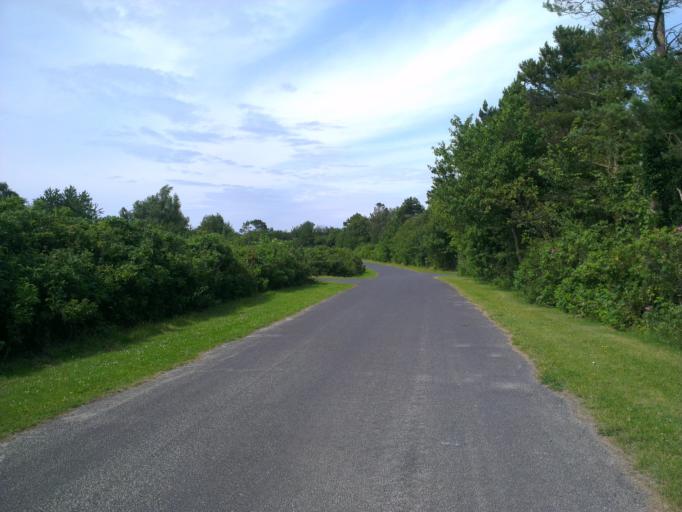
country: DK
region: Capital Region
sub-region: Halsnaes Kommune
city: Hundested
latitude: 55.9329
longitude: 11.9149
